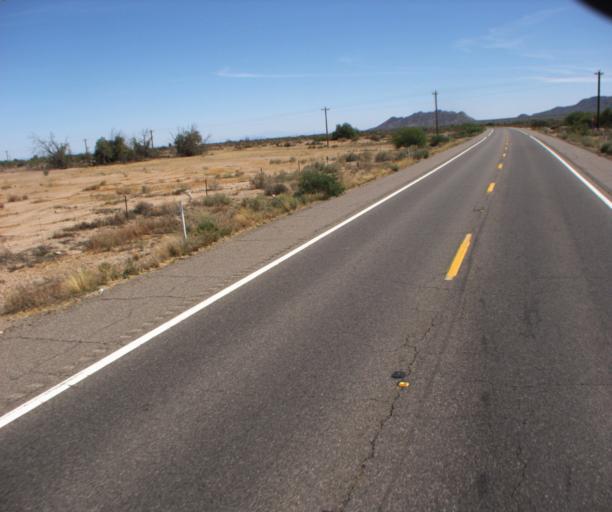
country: US
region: Arizona
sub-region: Pinal County
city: Sacaton
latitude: 33.0750
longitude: -111.7019
